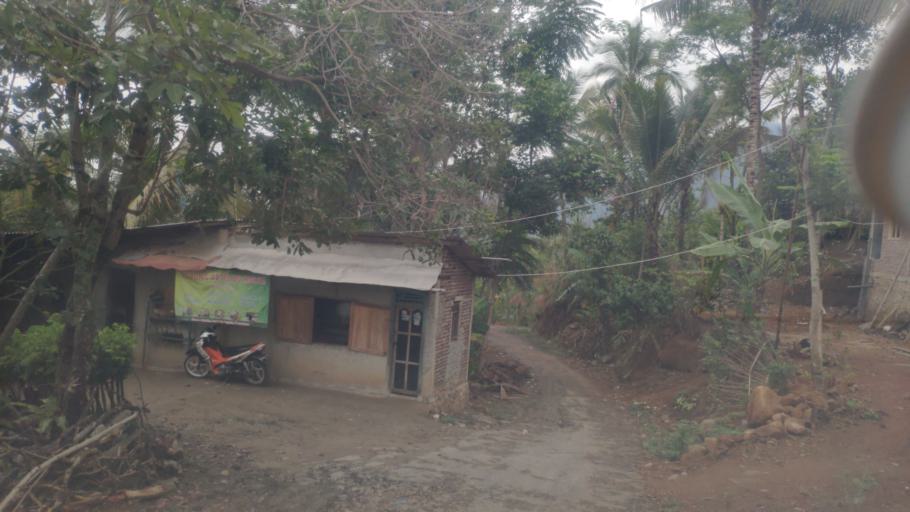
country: ID
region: Central Java
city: Purbalingga
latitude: -7.3074
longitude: 109.5802
